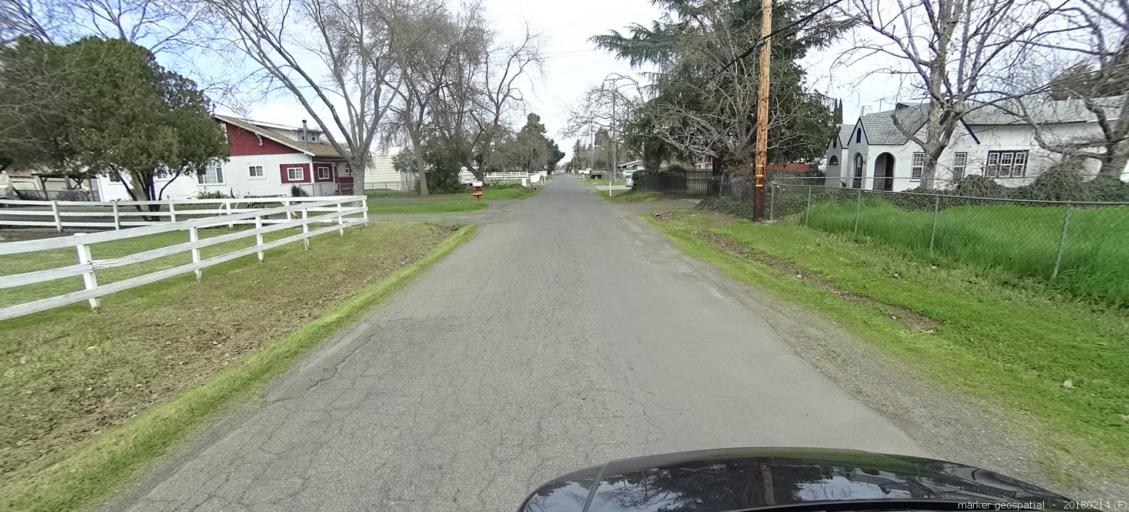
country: US
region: California
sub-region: Sacramento County
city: Rio Linda
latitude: 38.6798
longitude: -121.4661
